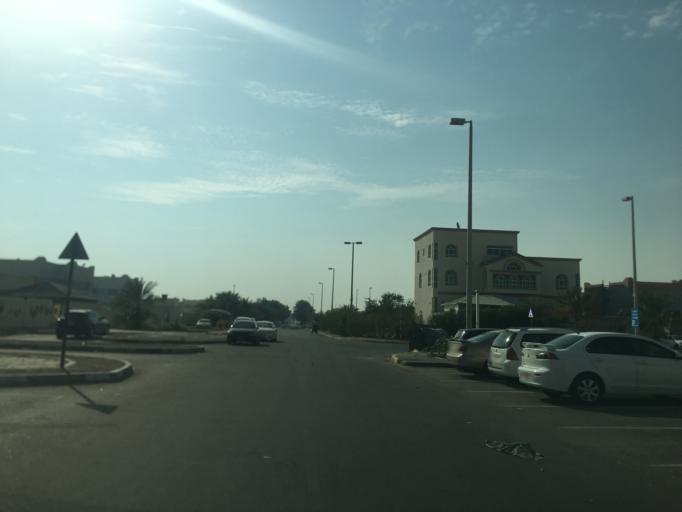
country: AE
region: Abu Dhabi
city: Abu Dhabi
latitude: 24.3000
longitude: 54.6507
